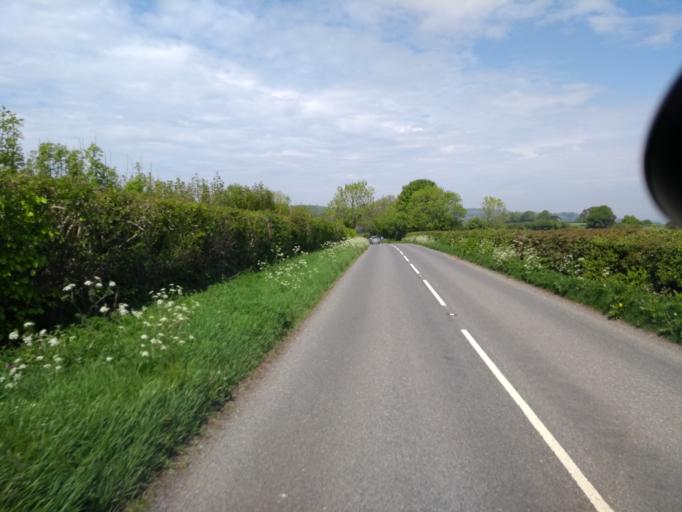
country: GB
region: England
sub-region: Somerset
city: Chard
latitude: 50.9073
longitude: -3.0059
